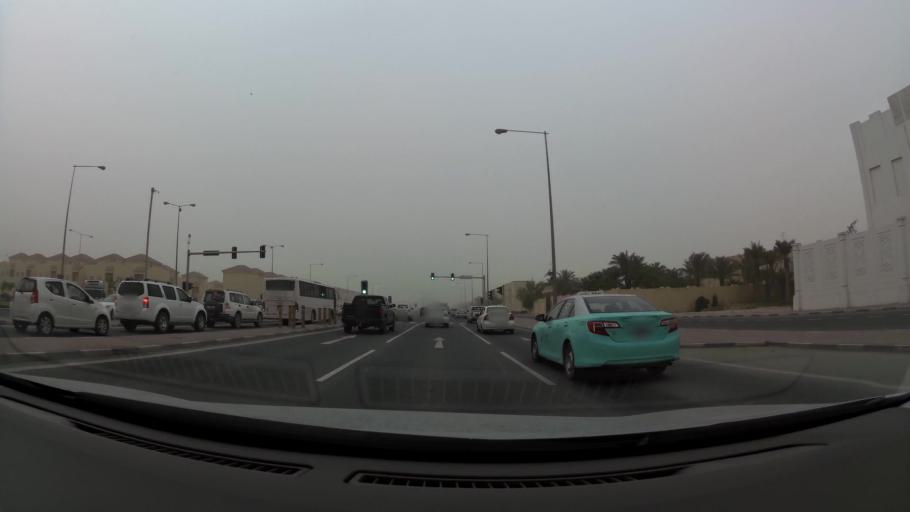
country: QA
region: Baladiyat ad Dawhah
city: Doha
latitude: 25.2448
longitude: 51.4933
